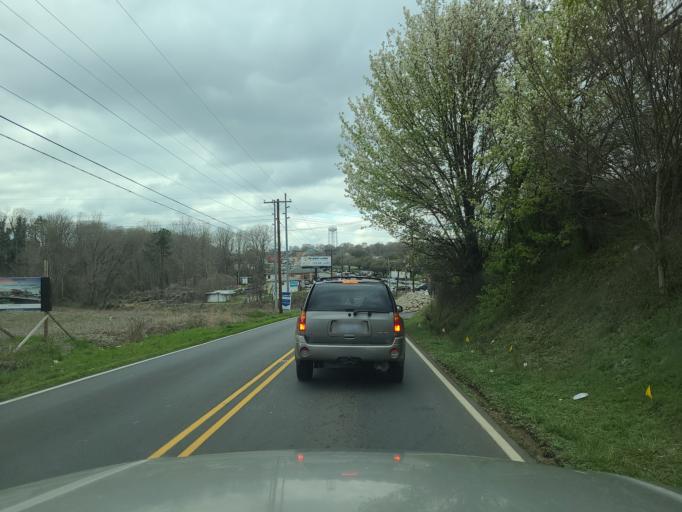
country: US
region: North Carolina
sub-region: Cleveland County
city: Shelby
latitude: 35.2736
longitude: -81.5310
